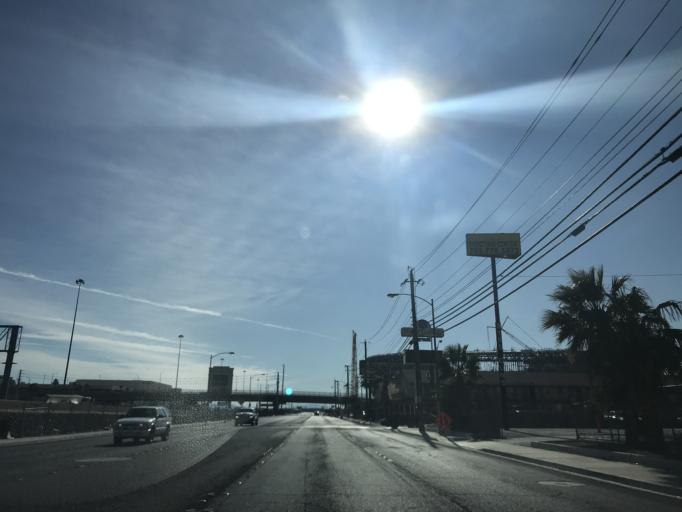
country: US
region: Nevada
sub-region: Clark County
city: Paradise
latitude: 36.0961
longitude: -115.1814
